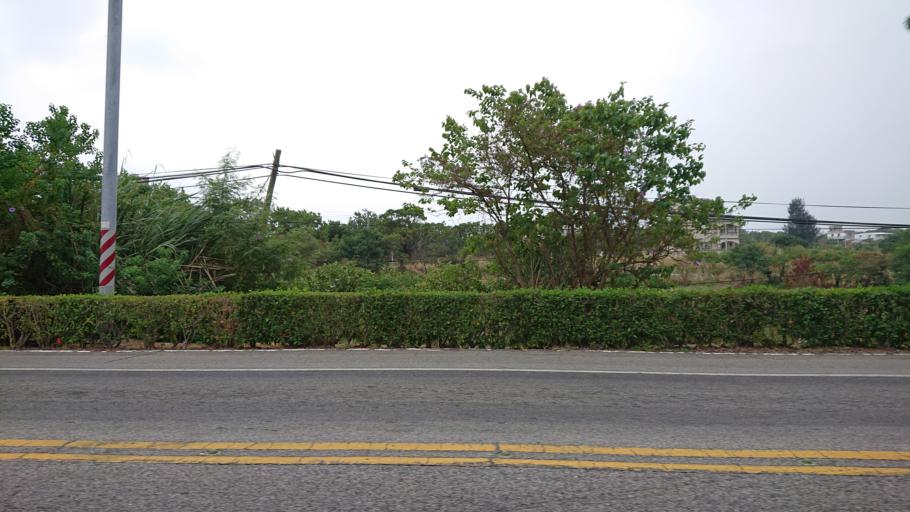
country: TW
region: Fukien
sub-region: Kinmen
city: Jincheng
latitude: 24.4440
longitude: 118.3878
